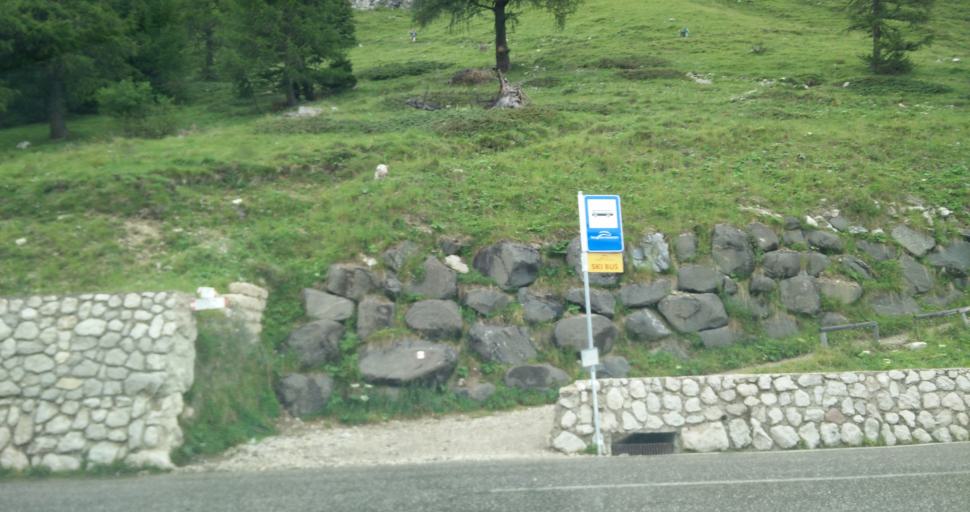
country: IT
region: Trentino-Alto Adige
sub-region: Bolzano
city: Corvara in Badia
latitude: 46.4641
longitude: 11.8624
